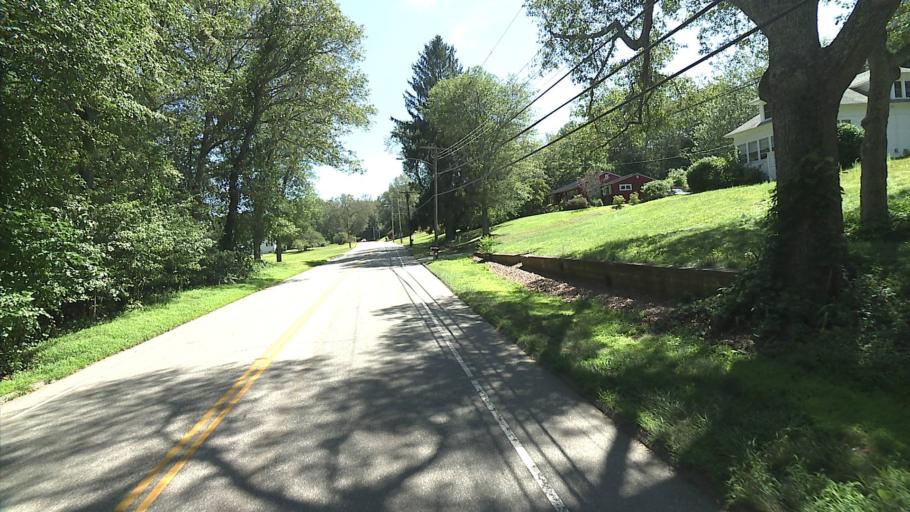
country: US
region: Connecticut
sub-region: New London County
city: Baltic
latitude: 41.6028
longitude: -72.0565
